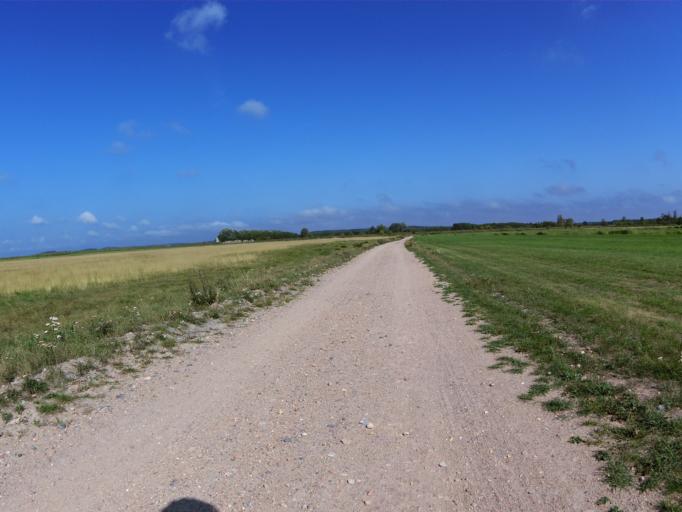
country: DE
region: Mecklenburg-Vorpommern
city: Loddin
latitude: 53.9761
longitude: 14.0513
